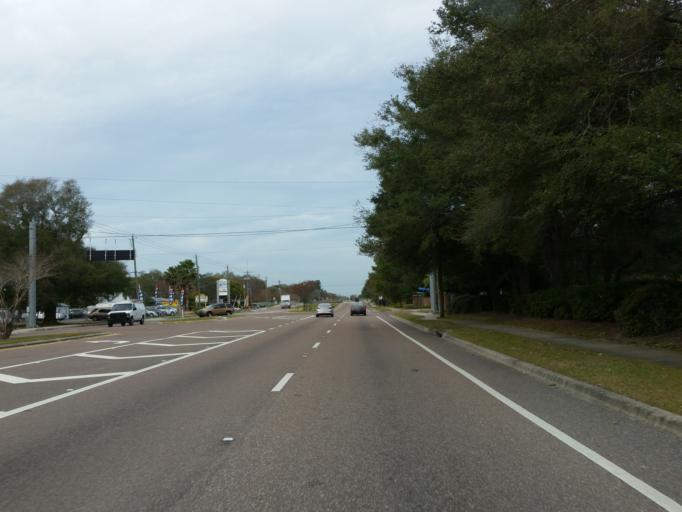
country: US
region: Florida
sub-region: Hillsborough County
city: Egypt Lake-Leto
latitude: 28.0404
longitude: -82.5186
